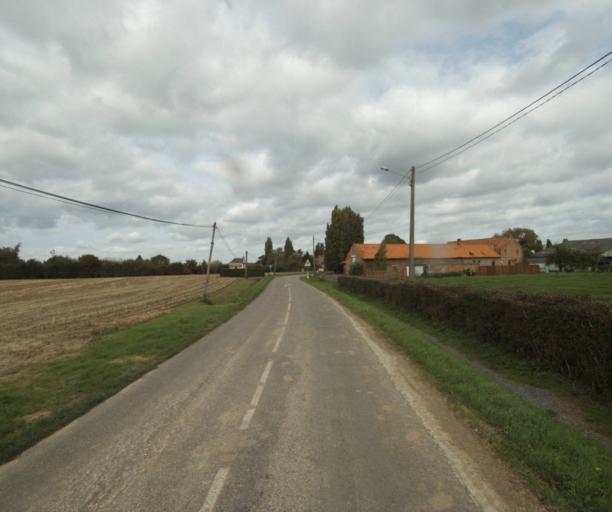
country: FR
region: Nord-Pas-de-Calais
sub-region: Departement du Nord
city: Erquinghem-Lys
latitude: 50.6706
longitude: 2.8456
